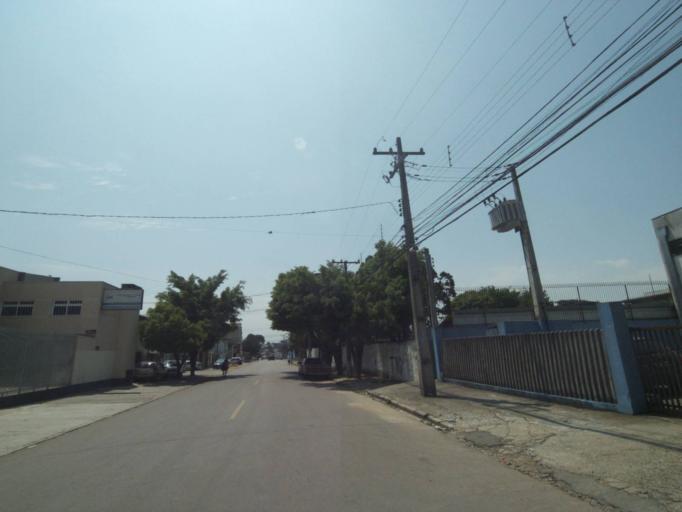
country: BR
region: Parana
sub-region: Curitiba
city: Curitiba
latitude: -25.4869
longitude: -49.3175
